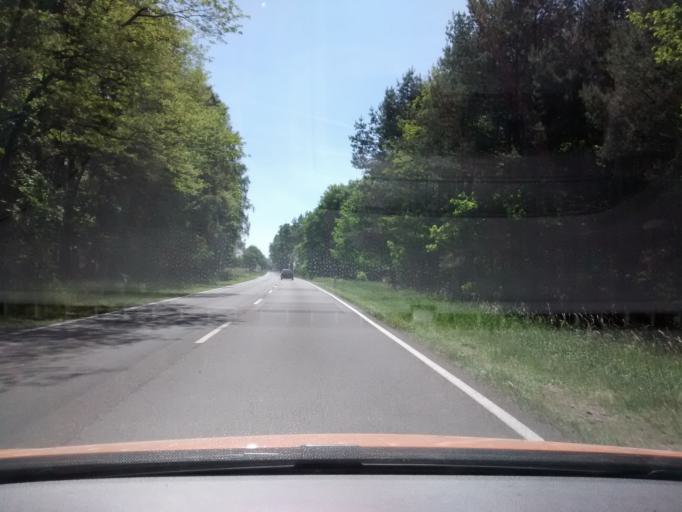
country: DE
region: Brandenburg
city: Storkow
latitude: 52.2974
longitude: 13.9031
